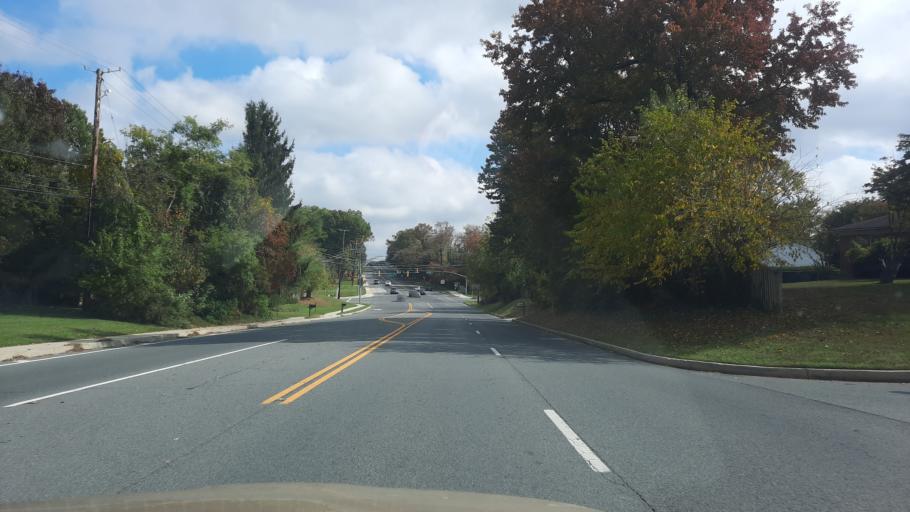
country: US
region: Maryland
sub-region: Montgomery County
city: Gaithersburg
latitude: 39.1487
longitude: -77.2397
